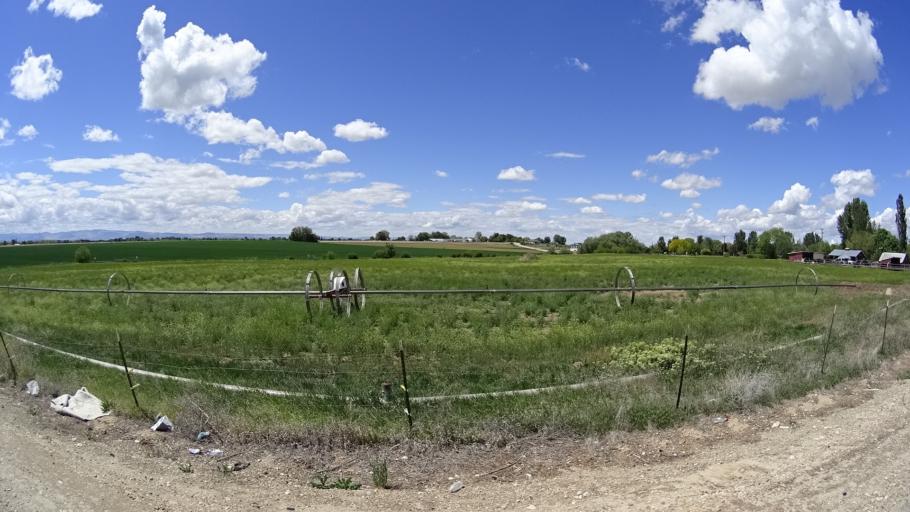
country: US
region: Idaho
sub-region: Ada County
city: Meridian
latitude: 43.5892
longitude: -116.4537
